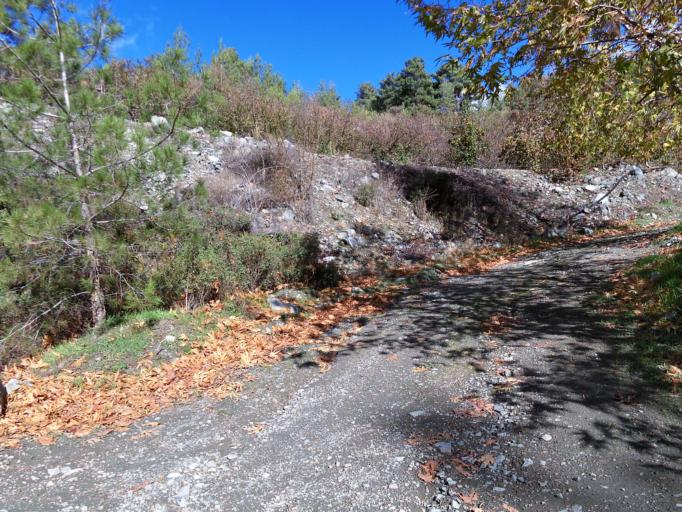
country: CY
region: Limassol
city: Kyperounta
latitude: 34.9297
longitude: 32.9467
